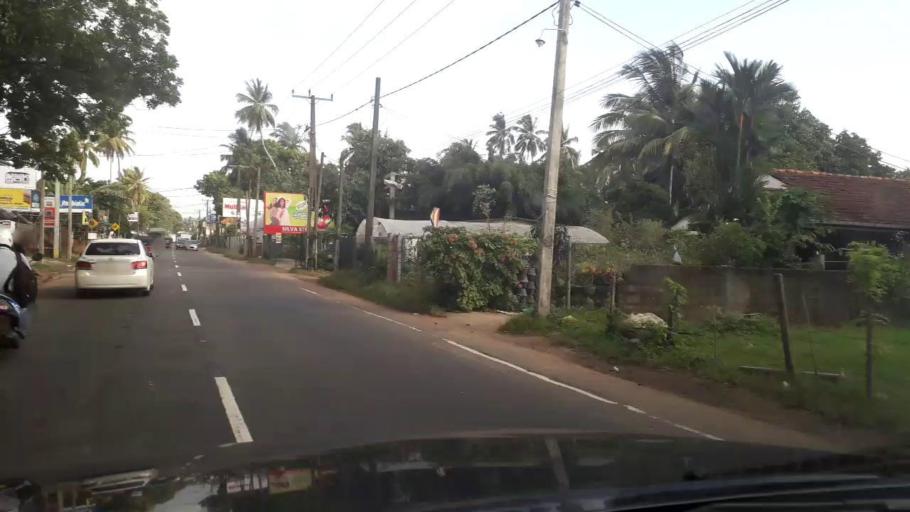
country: LK
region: Western
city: Beruwala
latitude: 6.5271
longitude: 79.9788
